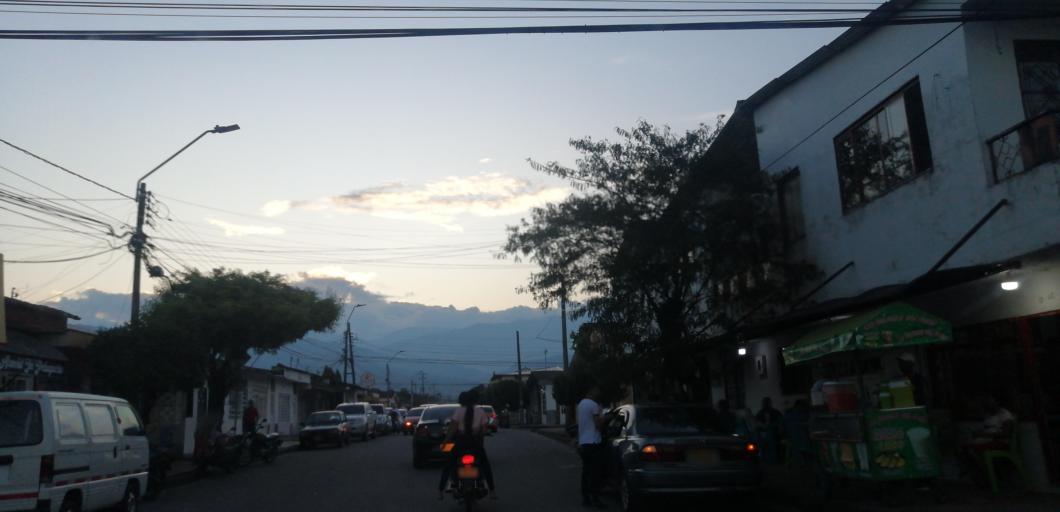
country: CO
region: Meta
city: Acacias
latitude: 3.9921
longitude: -73.7595
